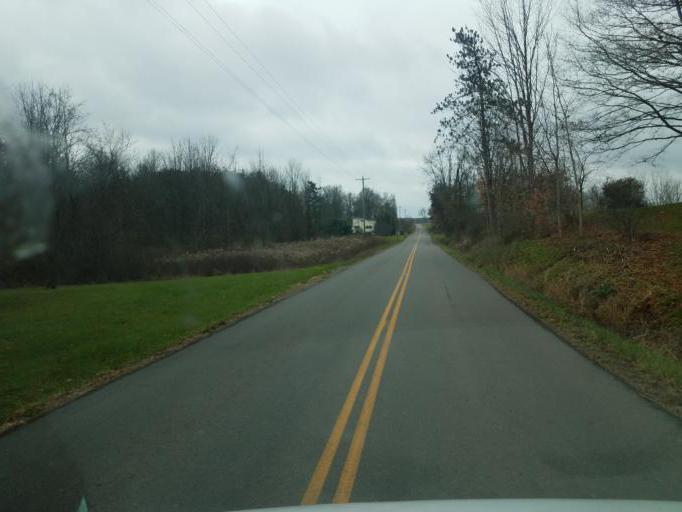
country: US
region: Ohio
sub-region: Knox County
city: Centerburg
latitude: 40.3167
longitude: -82.5921
